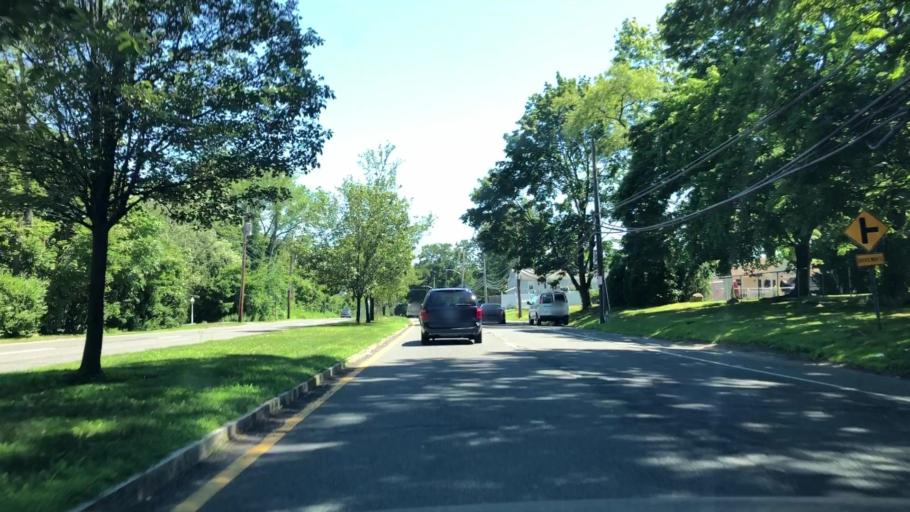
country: US
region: New York
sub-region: Westchester County
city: White Plains
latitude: 41.0049
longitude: -73.7508
